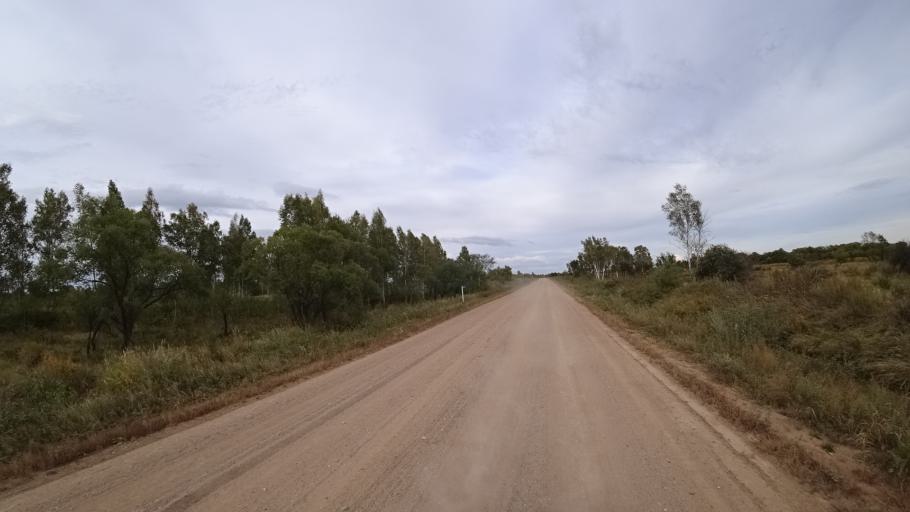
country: RU
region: Amur
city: Arkhara
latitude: 49.3500
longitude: 130.1292
